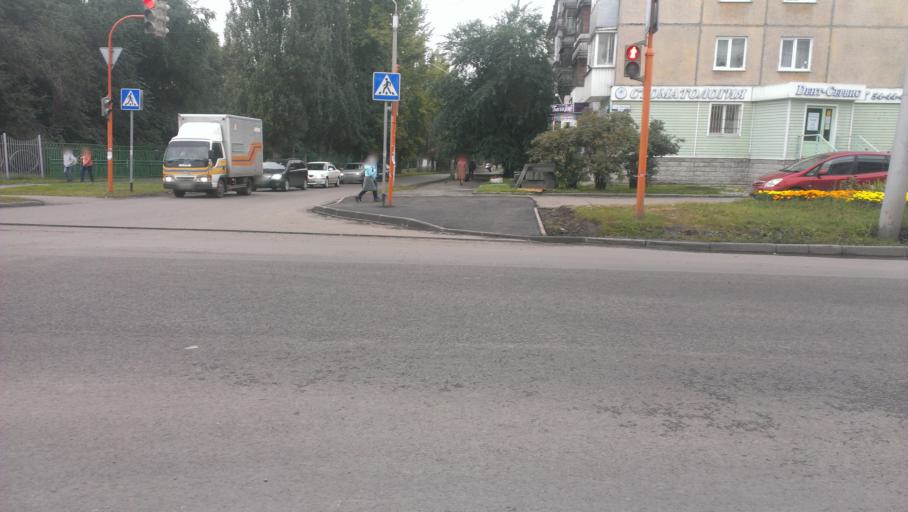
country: RU
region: Altai Krai
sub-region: Gorod Barnaulskiy
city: Barnaul
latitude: 53.3702
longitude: 83.6899
